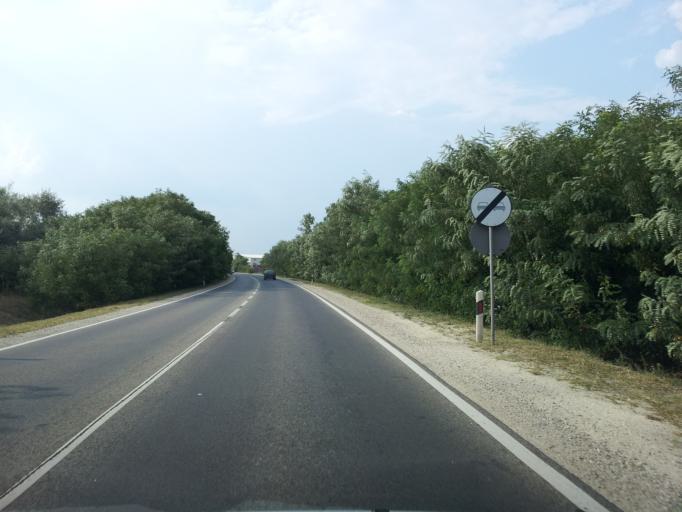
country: HU
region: Pest
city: Dunaharaszti
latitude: 47.3581
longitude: 19.1233
